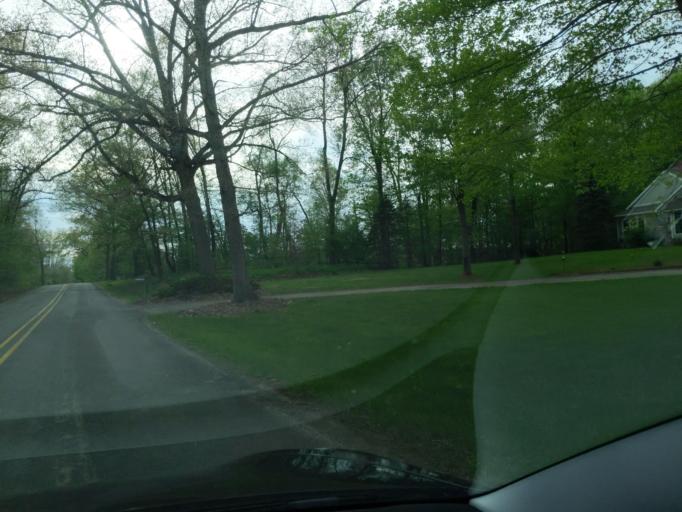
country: US
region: Michigan
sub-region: Ingham County
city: Stockbridge
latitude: 42.4392
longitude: -84.1447
